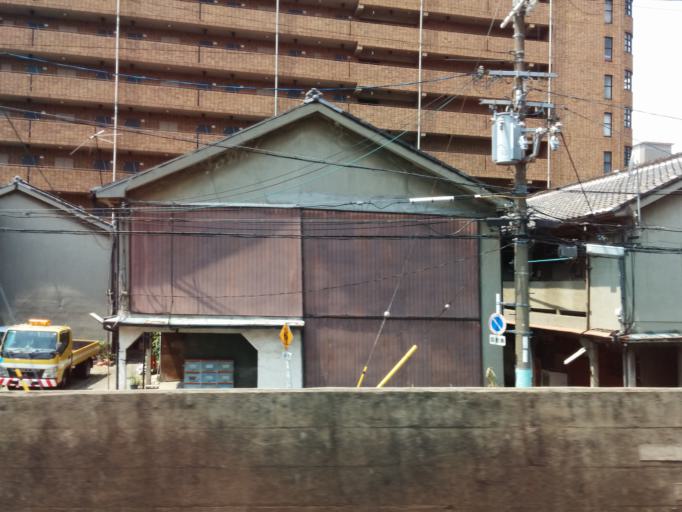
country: JP
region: Osaka
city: Osaka-shi
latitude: 34.7148
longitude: 135.5119
